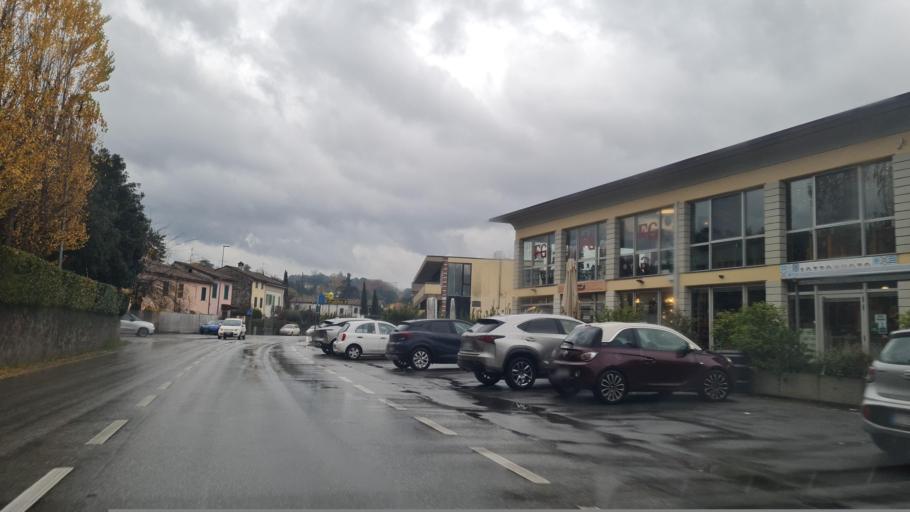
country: IT
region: Tuscany
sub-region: Provincia di Lucca
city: Lucca
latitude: 43.8602
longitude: 10.4949
